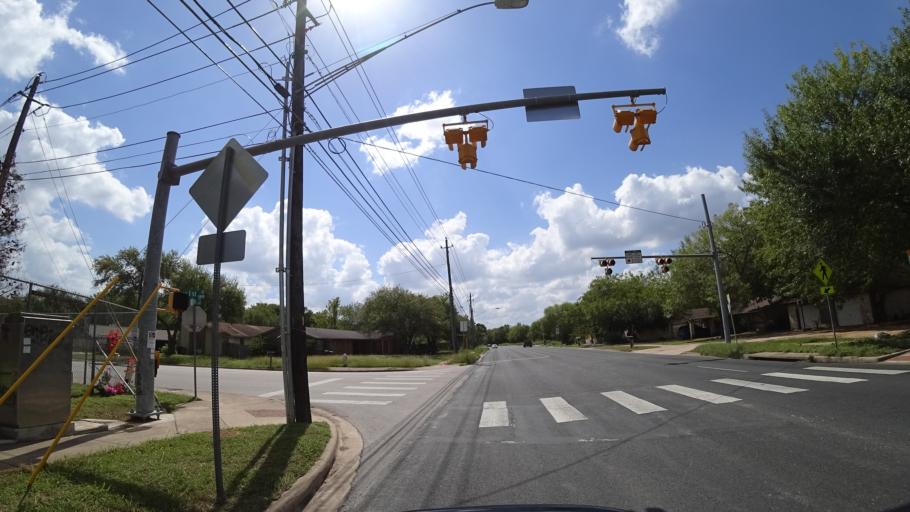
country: US
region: Texas
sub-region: Travis County
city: Onion Creek
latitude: 30.1945
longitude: -97.7894
